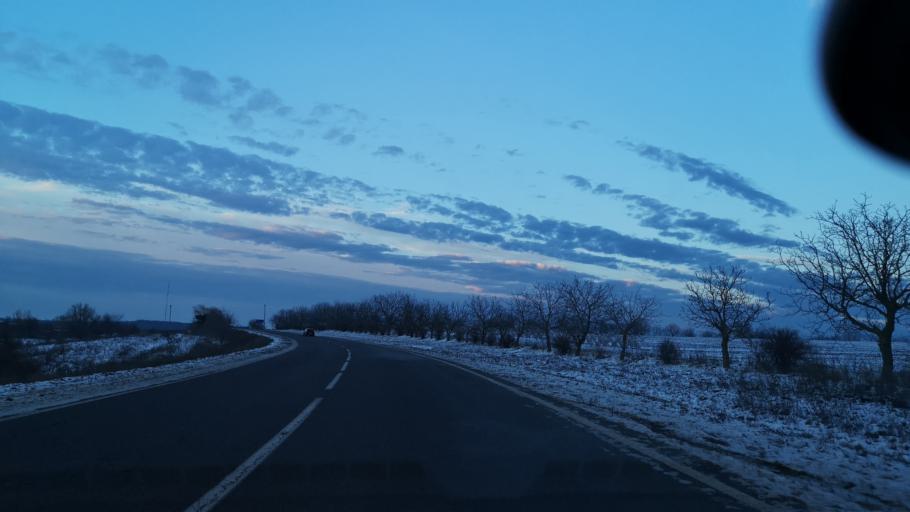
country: MD
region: Rezina
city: Saharna
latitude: 47.6308
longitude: 28.8374
